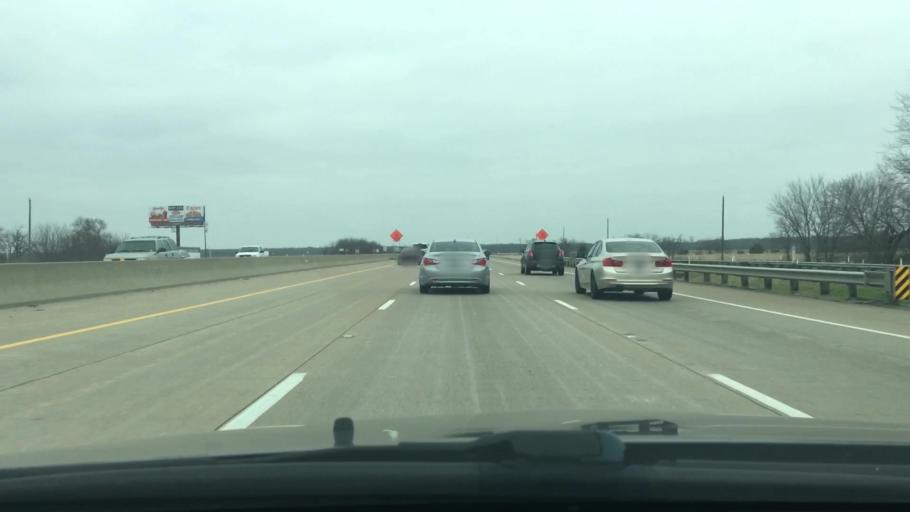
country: US
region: Texas
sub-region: Navarro County
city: Corsicana
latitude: 32.1798
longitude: -96.4714
